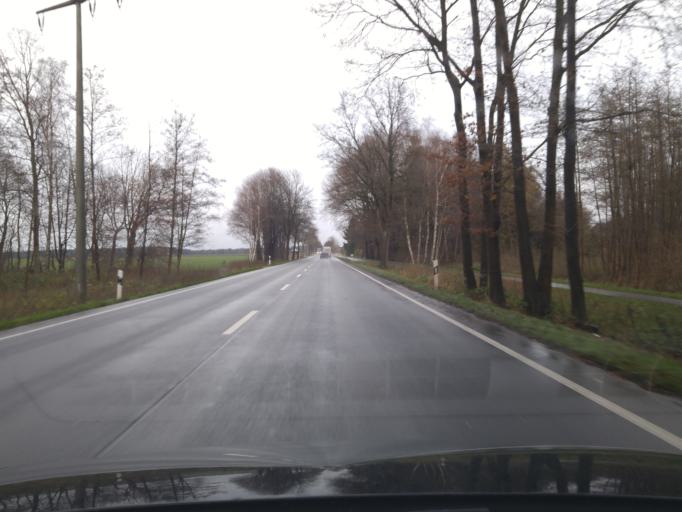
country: DE
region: Lower Saxony
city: Gross Oesingen
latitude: 52.6582
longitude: 10.4648
